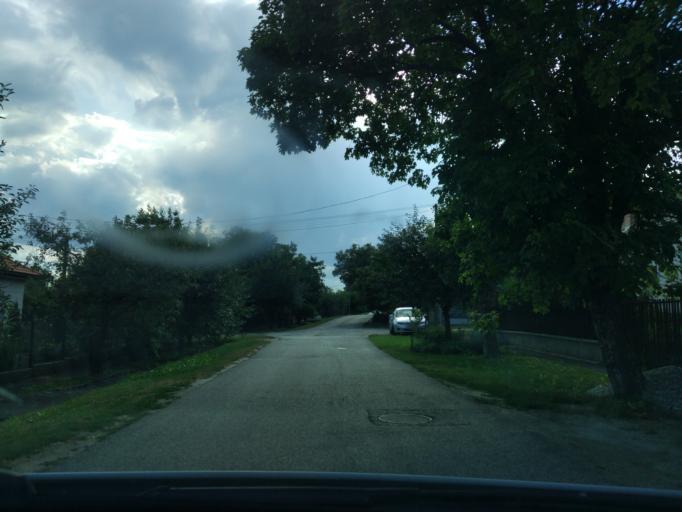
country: HU
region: Veszprem
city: Varpalota
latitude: 47.2024
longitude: 18.1709
